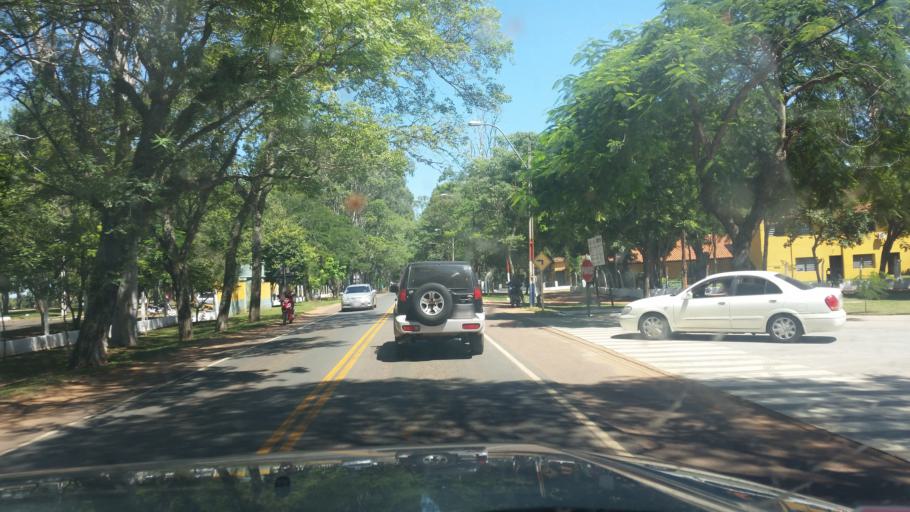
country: PY
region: Misiones
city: San Juan Bautista
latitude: -26.6679
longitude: -57.1339
